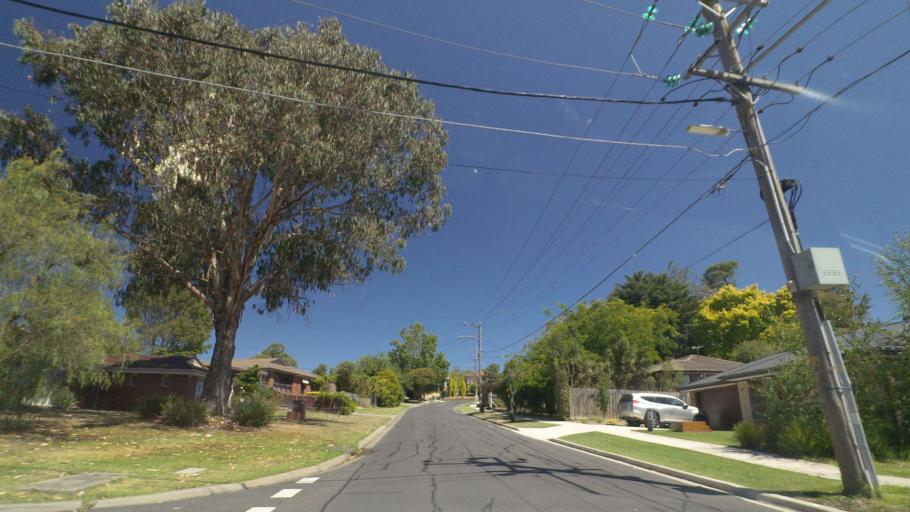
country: AU
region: Victoria
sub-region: Yarra Ranges
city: Lilydale
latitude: -37.7557
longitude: 145.3308
